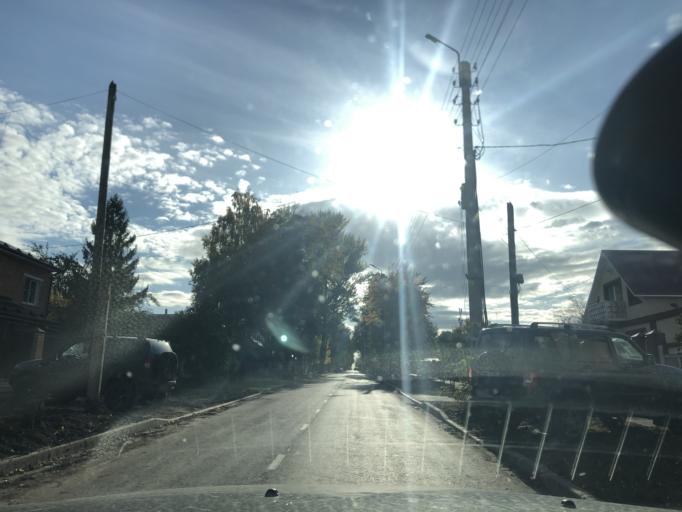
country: RU
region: Tula
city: Kireyevsk
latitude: 53.9388
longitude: 37.9352
